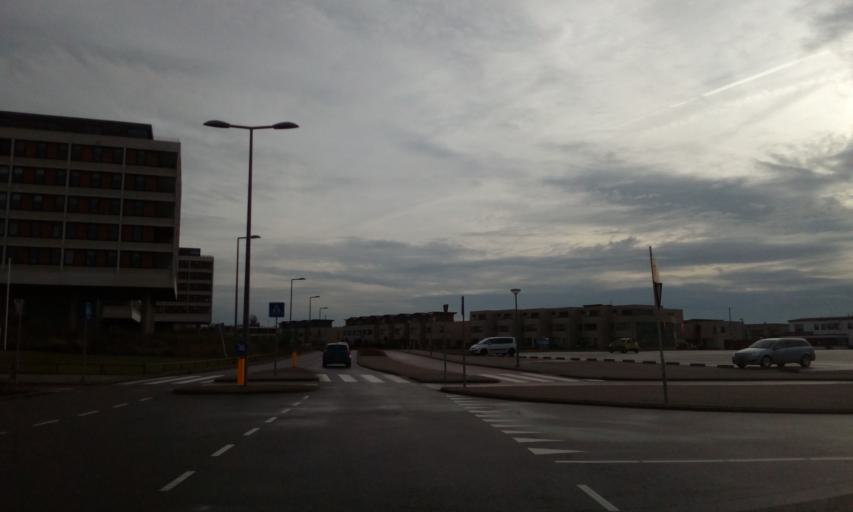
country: NL
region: South Holland
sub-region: Gemeente Rotterdam
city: Hoek van Holland
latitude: 51.9830
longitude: 4.1131
